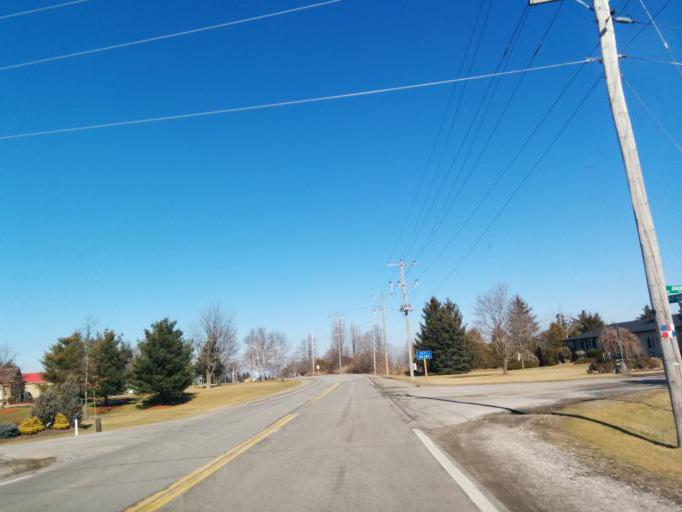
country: CA
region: Ontario
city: Brant
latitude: 43.0196
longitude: -80.3267
